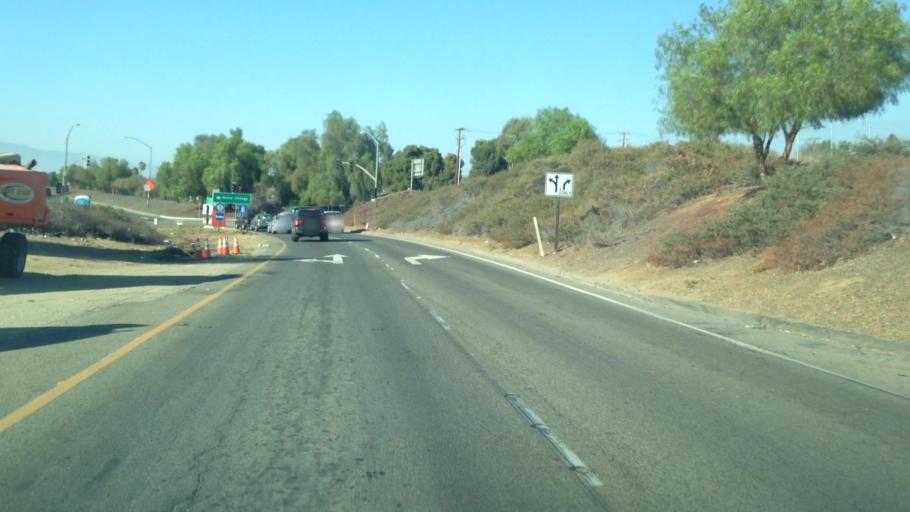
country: US
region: California
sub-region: Riverside County
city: Norco
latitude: 33.9089
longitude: -117.5581
